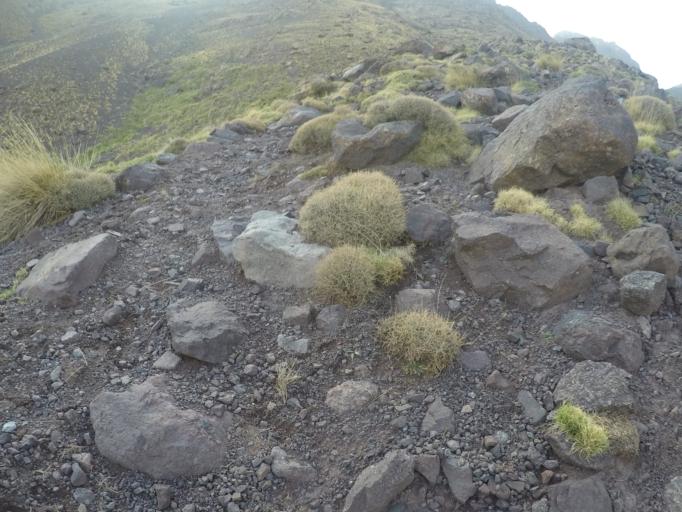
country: MA
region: Marrakech-Tensift-Al Haouz
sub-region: Al-Haouz
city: Moulay Brahim
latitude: 31.0858
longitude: -7.9718
